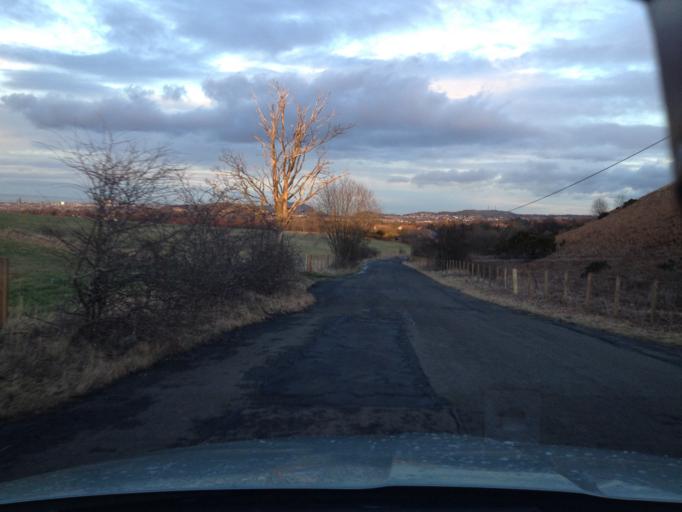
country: GB
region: Scotland
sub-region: Edinburgh
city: Colinton
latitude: 55.8991
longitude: -3.2743
